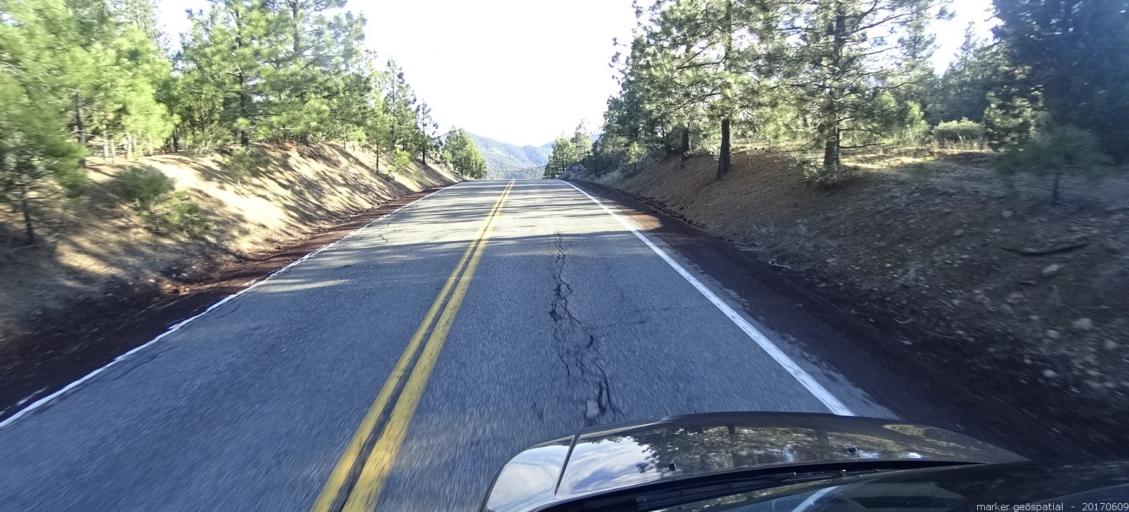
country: US
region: California
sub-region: Siskiyou County
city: Weed
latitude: 41.4356
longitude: -122.6392
